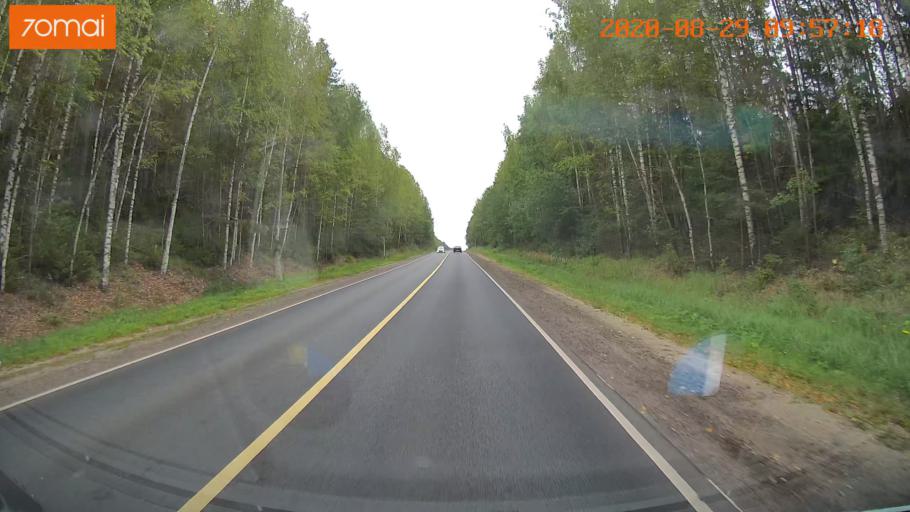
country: RU
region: Ivanovo
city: Zarechnyy
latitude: 57.4168
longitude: 42.3102
